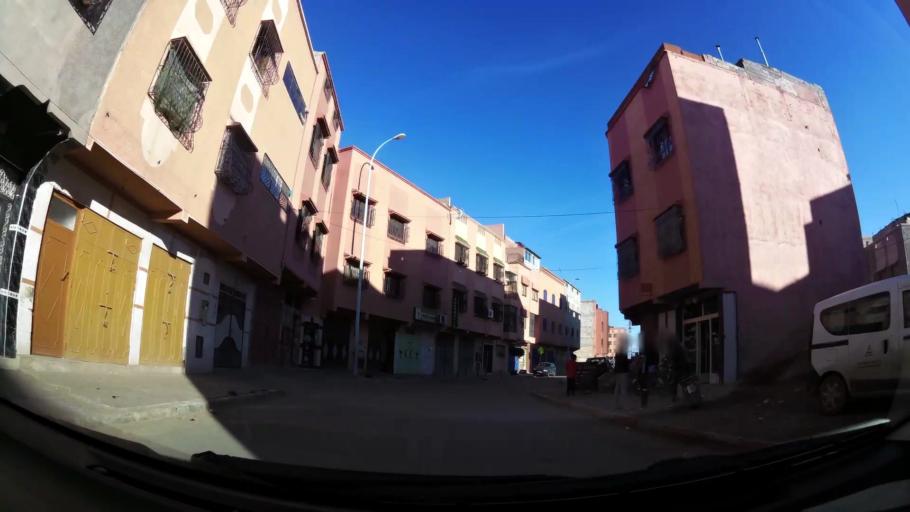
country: MA
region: Marrakech-Tensift-Al Haouz
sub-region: Marrakech
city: Marrakesh
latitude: 31.6164
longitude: -8.0658
